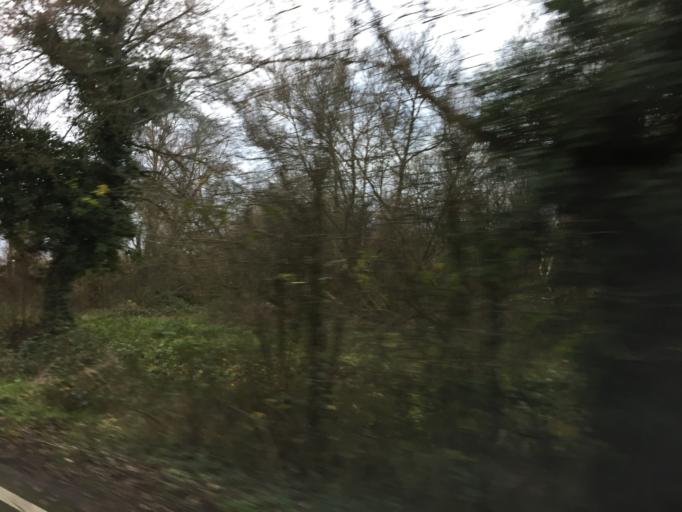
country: GB
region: Wales
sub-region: Newport
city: Bishton
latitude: 51.5719
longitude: -2.8687
